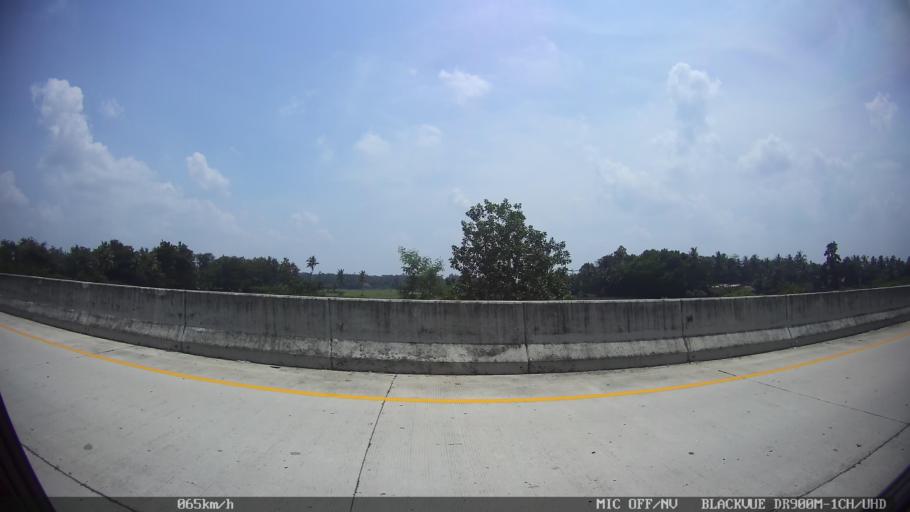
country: ID
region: Lampung
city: Natar
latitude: -5.2929
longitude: 105.2332
